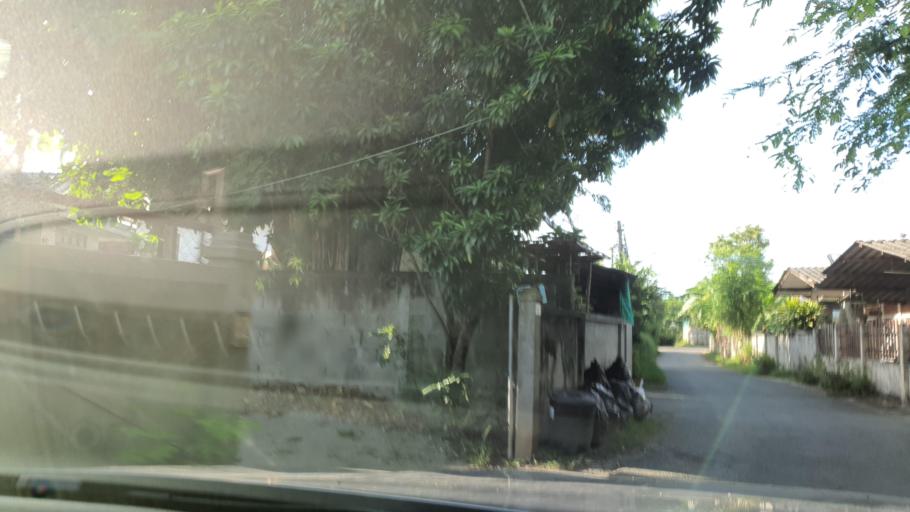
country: TH
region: Chiang Mai
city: San Kamphaeng
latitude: 18.7427
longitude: 99.1112
